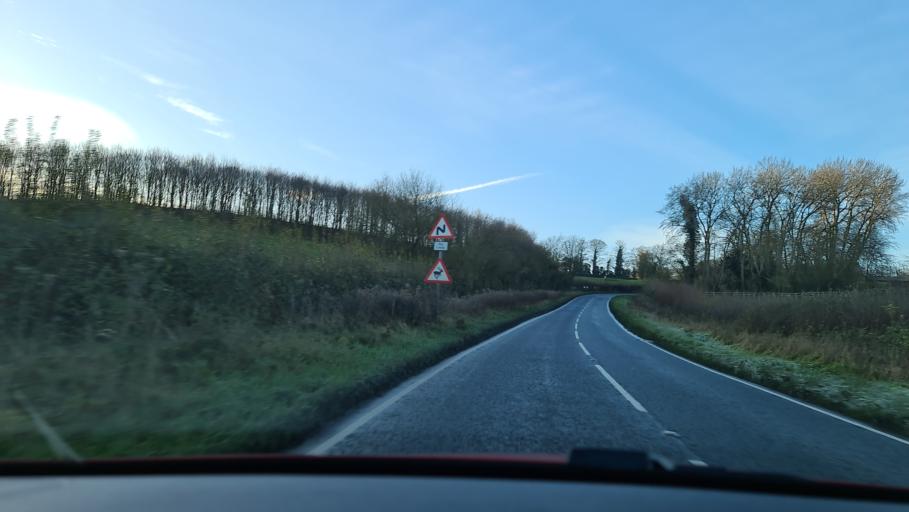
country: GB
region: England
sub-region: Buckinghamshire
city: Waddesdon
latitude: 51.8362
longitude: -0.9033
